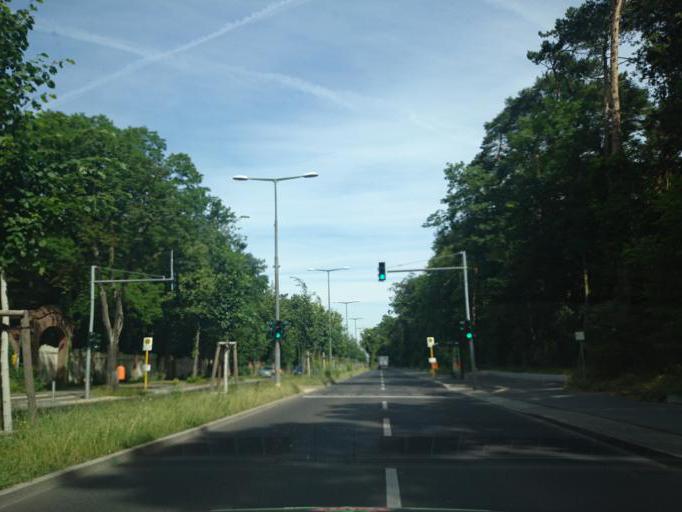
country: DE
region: Berlin
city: Lichtenrade
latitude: 52.3776
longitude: 13.4171
